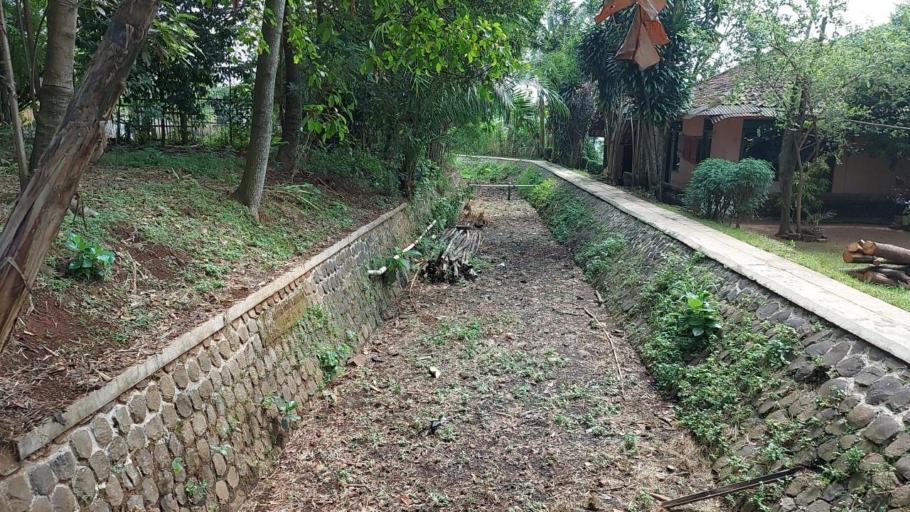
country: ID
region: West Java
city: Bogor
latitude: -6.5412
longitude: 106.8169
